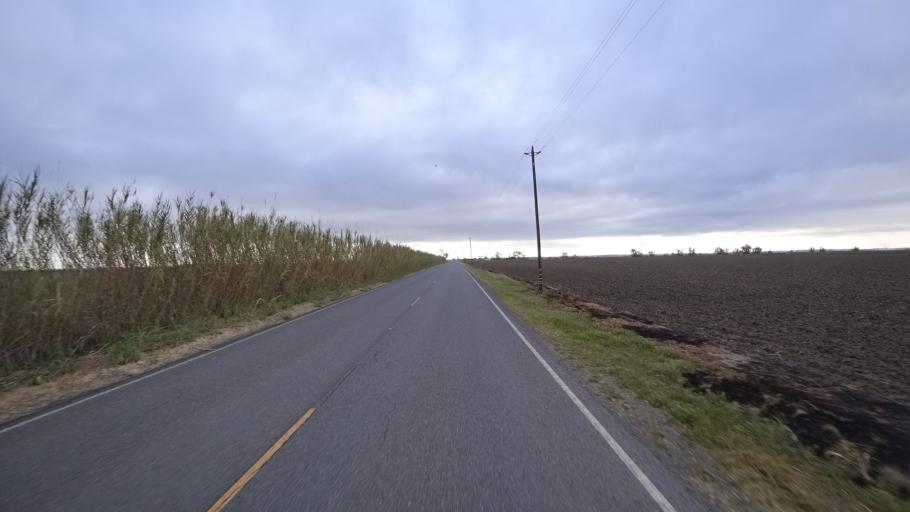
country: US
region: California
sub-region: Glenn County
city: Willows
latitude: 39.4064
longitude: -122.0866
